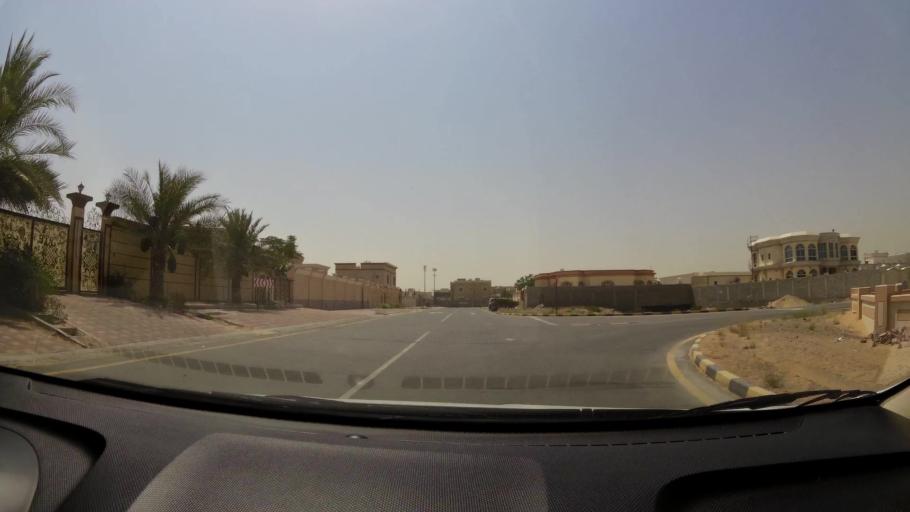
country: AE
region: Ajman
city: Ajman
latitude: 25.4233
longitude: 55.5201
